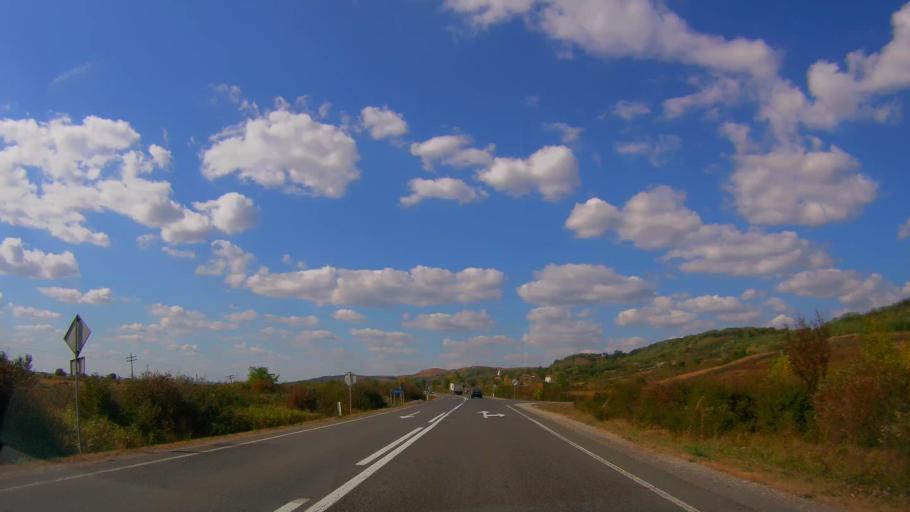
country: RO
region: Salaj
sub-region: Comuna Bocsa
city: Bocsa
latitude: 47.3130
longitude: 22.9135
